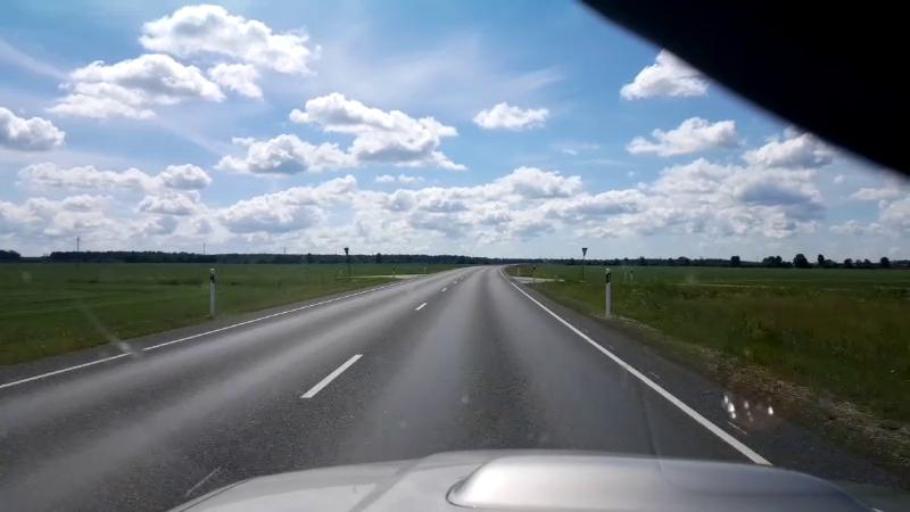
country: EE
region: Jaervamaa
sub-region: Jaerva-Jaani vald
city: Jarva-Jaani
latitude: 59.1499
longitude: 25.7699
